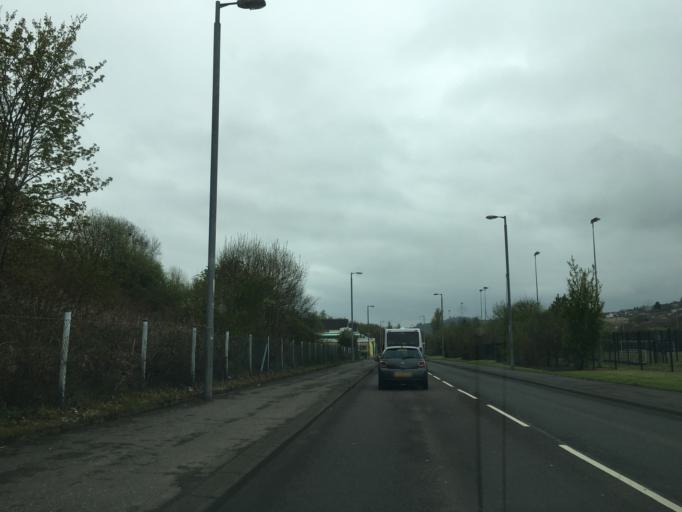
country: GB
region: Scotland
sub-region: Inverclyde
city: Gourock
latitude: 55.9390
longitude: -4.8091
